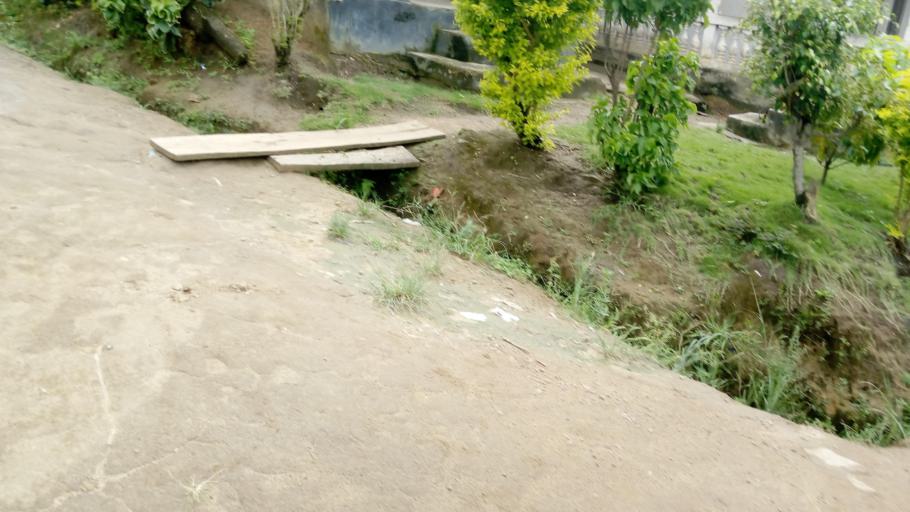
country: SL
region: Northern Province
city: Makeni
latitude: 8.8863
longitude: -12.0281
